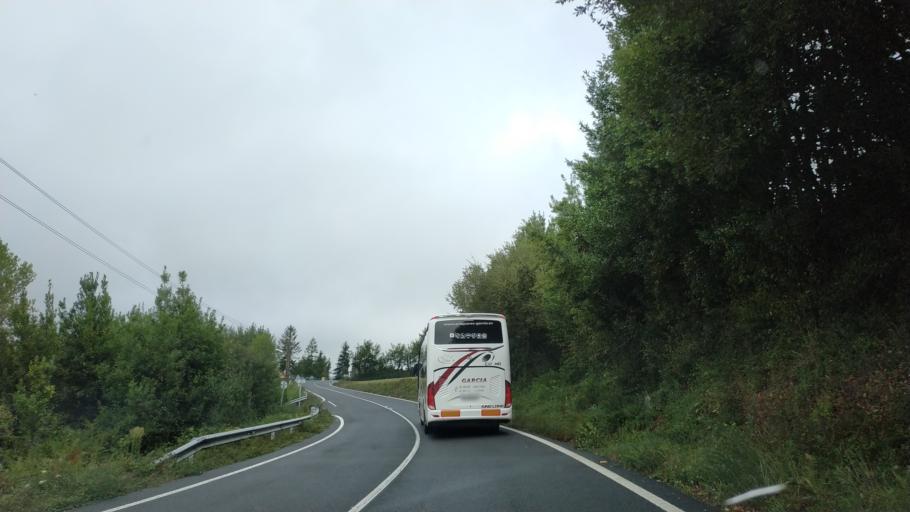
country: ES
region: Galicia
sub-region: Provincia da Coruna
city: Negreira
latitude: 42.9346
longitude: -8.7343
